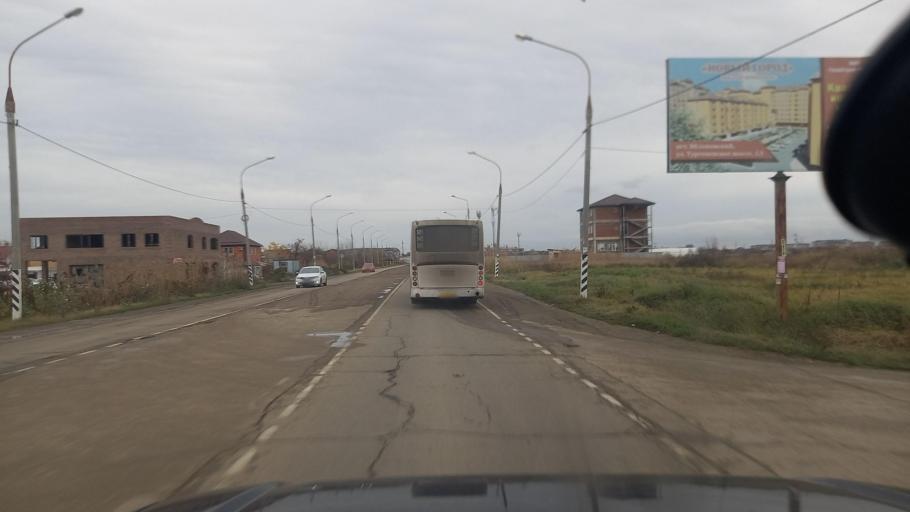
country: RU
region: Adygeya
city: Yablonovskiy
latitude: 44.9805
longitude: 38.9244
